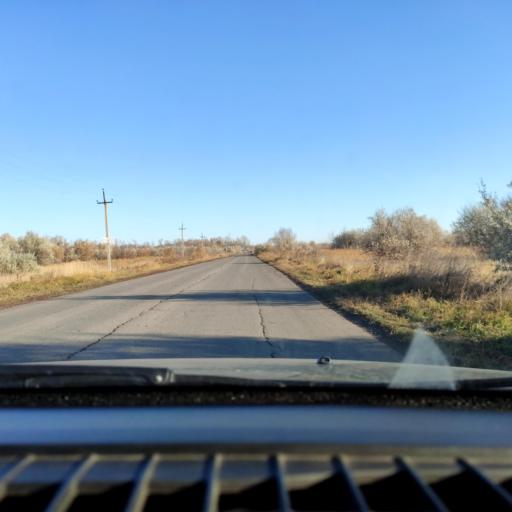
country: RU
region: Samara
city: Tol'yatti
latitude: 53.6352
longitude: 49.3077
